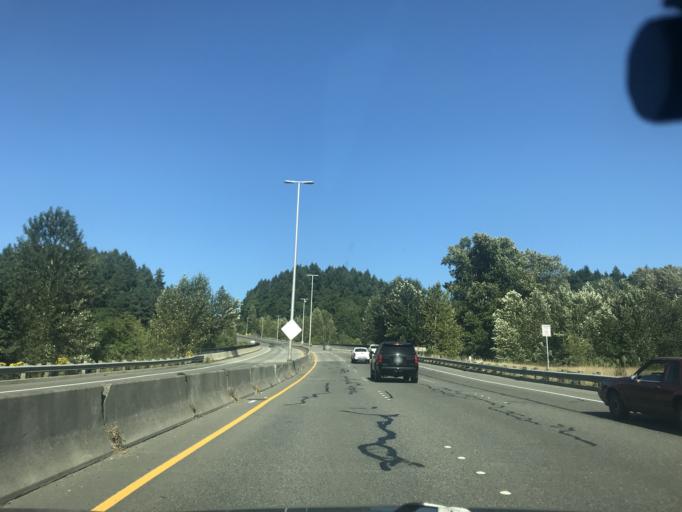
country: US
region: Washington
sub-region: King County
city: Kent
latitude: 47.3539
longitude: -122.2113
